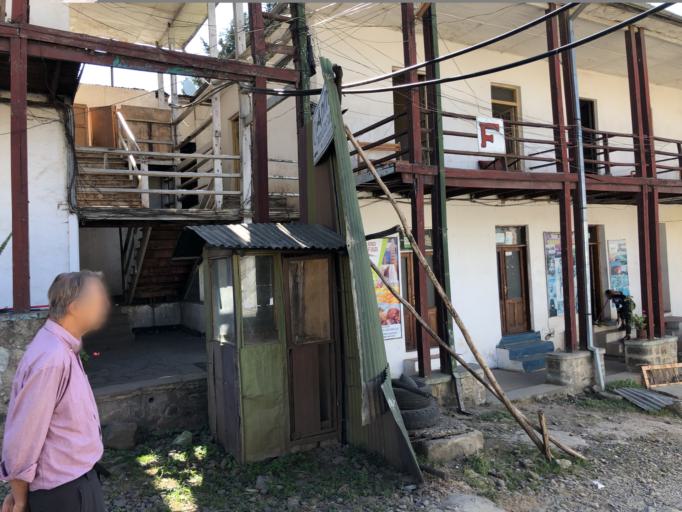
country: ET
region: Adis Abeba
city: Addis Ababa
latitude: 9.0302
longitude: 38.7541
